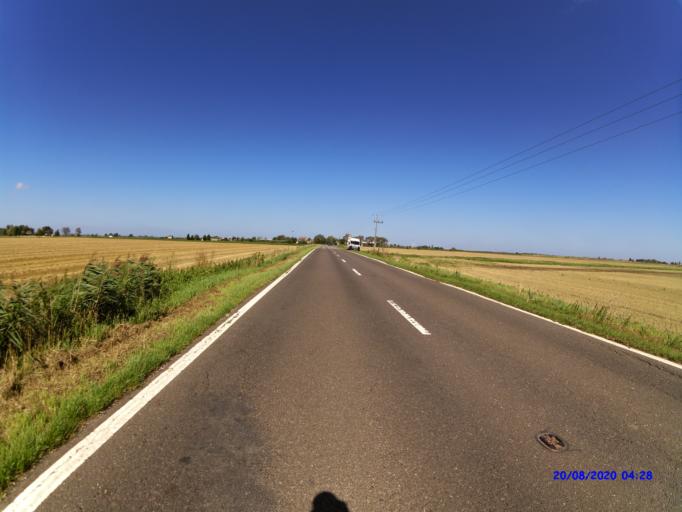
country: GB
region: England
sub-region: Cambridgeshire
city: Whittlesey
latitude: 52.5058
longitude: -0.1359
